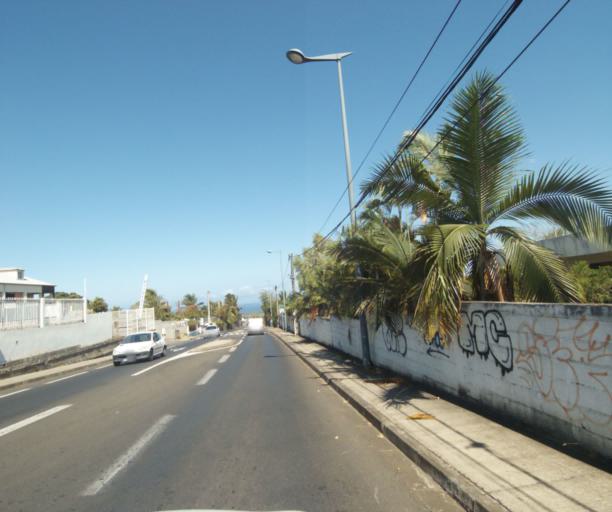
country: RE
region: Reunion
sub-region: Reunion
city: La Possession
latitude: -20.9780
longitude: 55.3240
